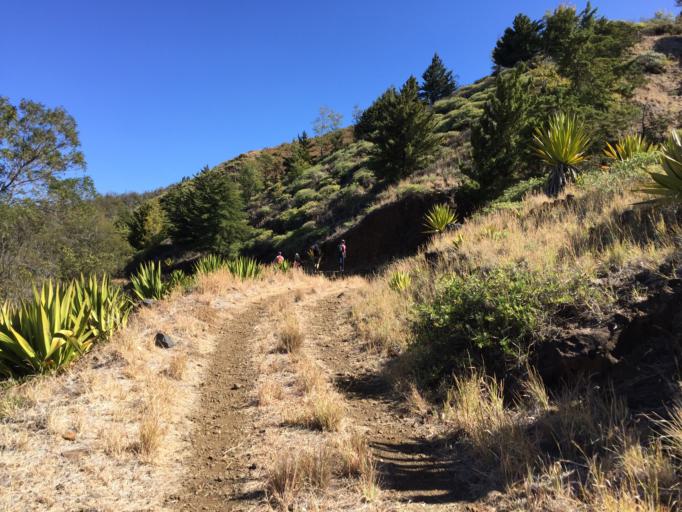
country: CV
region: Mosteiros
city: Porto dos Mosteiros
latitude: 15.0060
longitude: -24.3566
